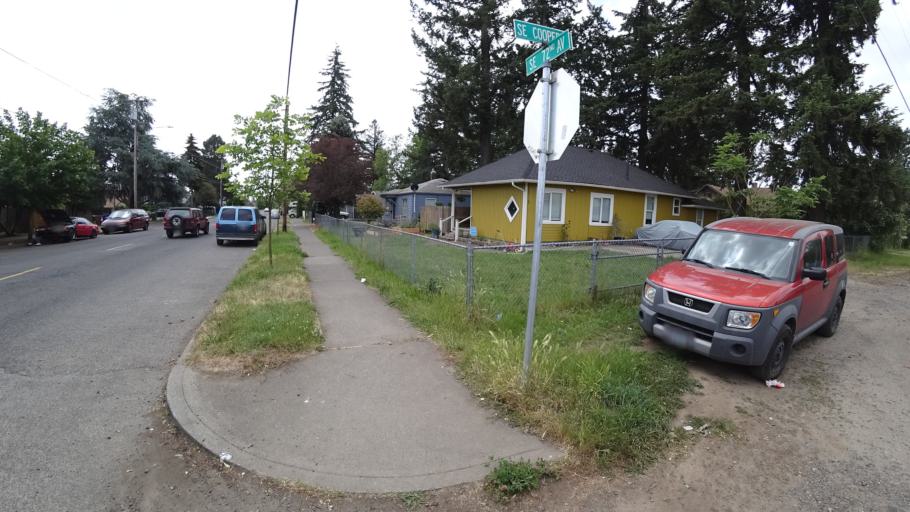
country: US
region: Oregon
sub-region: Multnomah County
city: Lents
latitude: 45.4735
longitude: -122.5895
